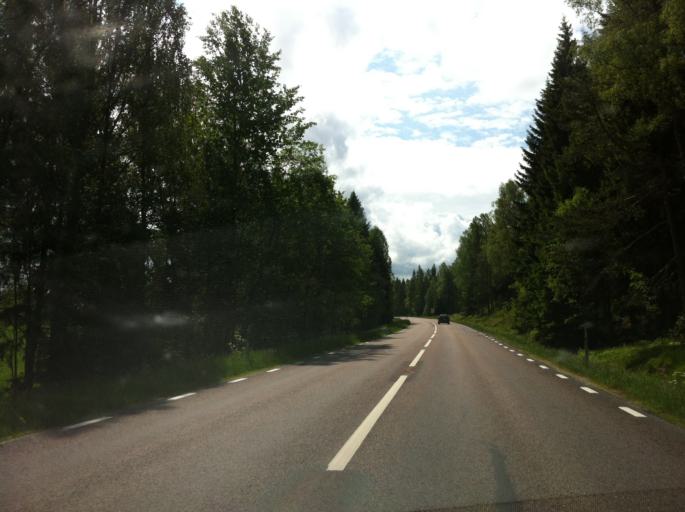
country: SE
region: Vaermland
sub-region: Karlstads Kommun
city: Edsvalla
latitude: 59.5486
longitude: 13.1950
